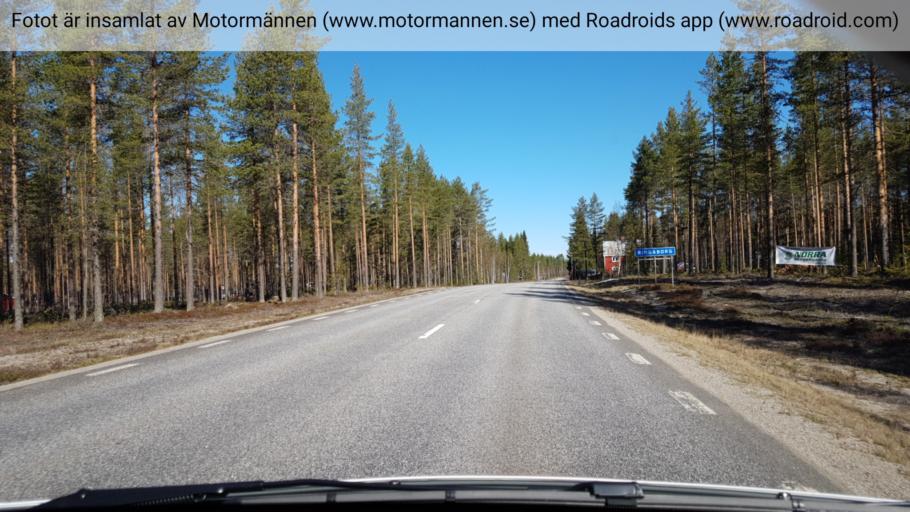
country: SE
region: Vaesterbotten
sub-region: Lycksele Kommun
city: Lycksele
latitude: 64.5286
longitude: 18.7728
